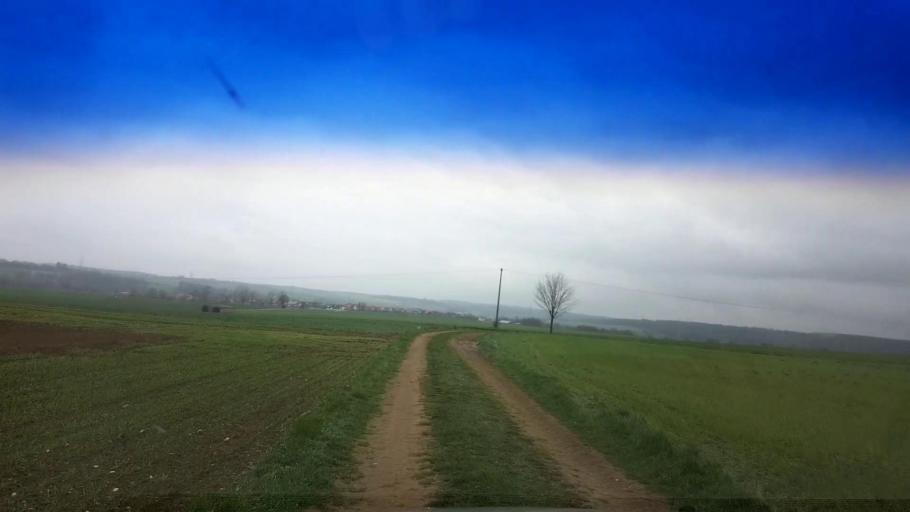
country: DE
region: Bavaria
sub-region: Upper Franconia
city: Schesslitz
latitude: 49.9495
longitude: 11.0125
